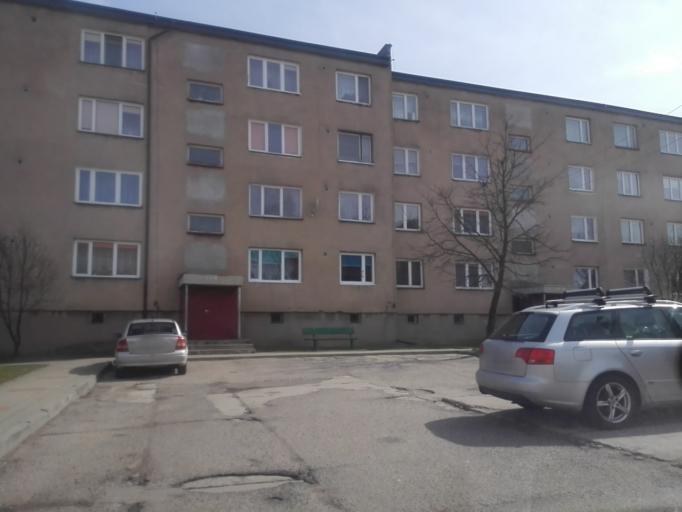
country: PL
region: Podlasie
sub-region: Powiat sejnenski
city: Sejny
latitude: 54.1054
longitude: 23.3409
